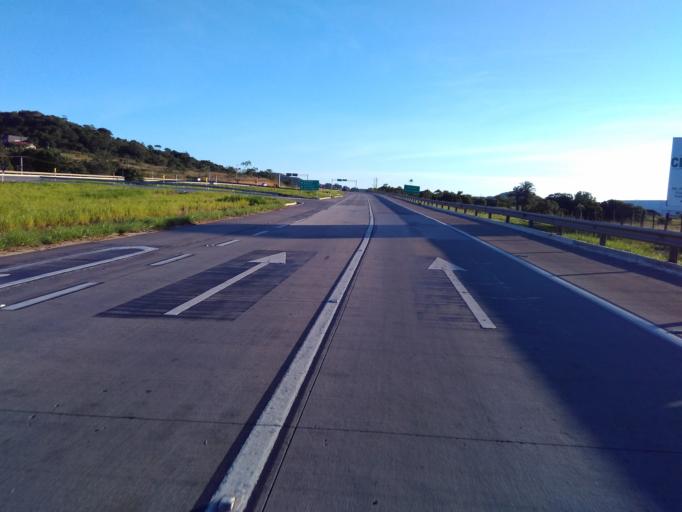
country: BR
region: Sergipe
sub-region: Nossa Senhora Do Socorro
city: Nossa Senhora do Socorro
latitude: -10.9178
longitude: -37.1678
